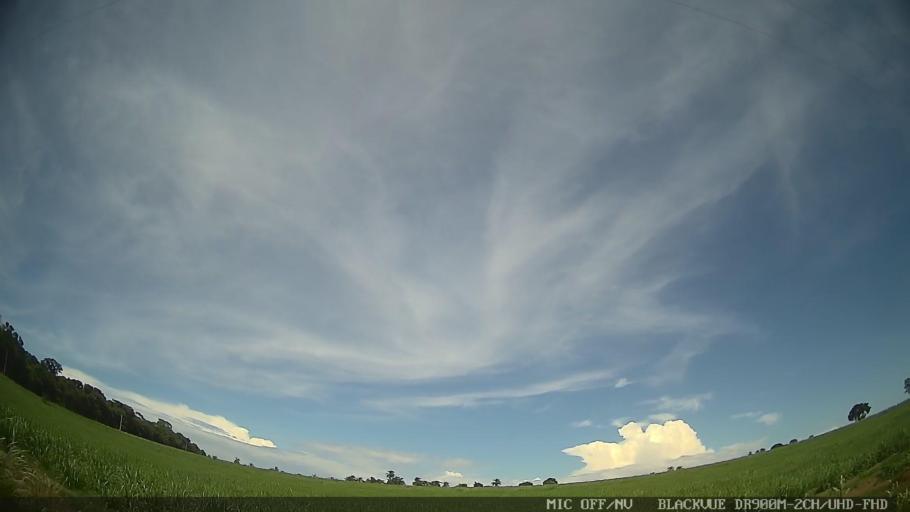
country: BR
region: Sao Paulo
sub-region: Jaguariuna
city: Jaguariuna
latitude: -22.6162
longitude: -47.0391
